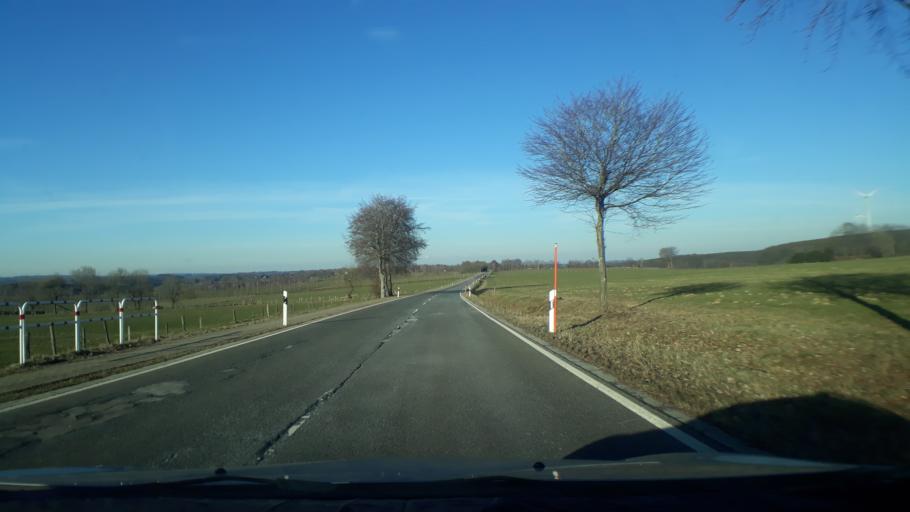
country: DE
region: North Rhine-Westphalia
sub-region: Regierungsbezirk Koln
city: Monschau
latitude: 50.5328
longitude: 6.2762
